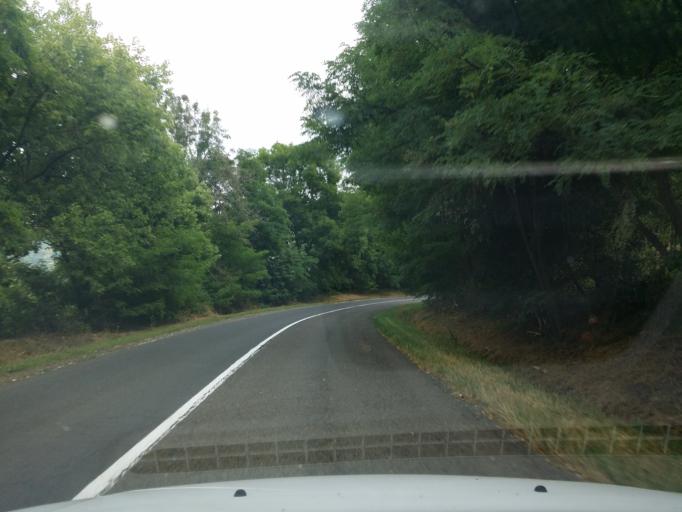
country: HU
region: Nograd
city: Bercel
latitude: 47.9219
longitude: 19.3667
